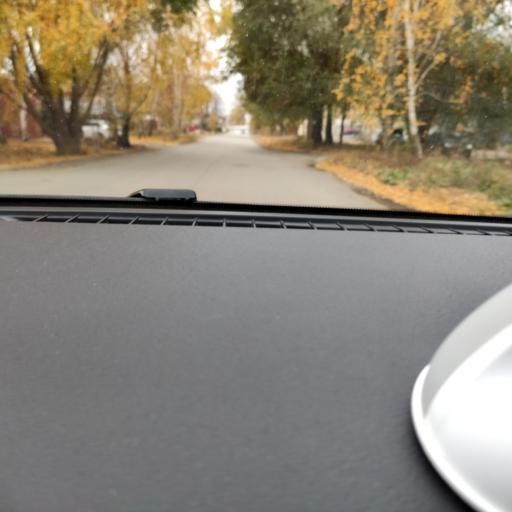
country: RU
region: Samara
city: Petra-Dubrava
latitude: 53.2431
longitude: 50.3123
